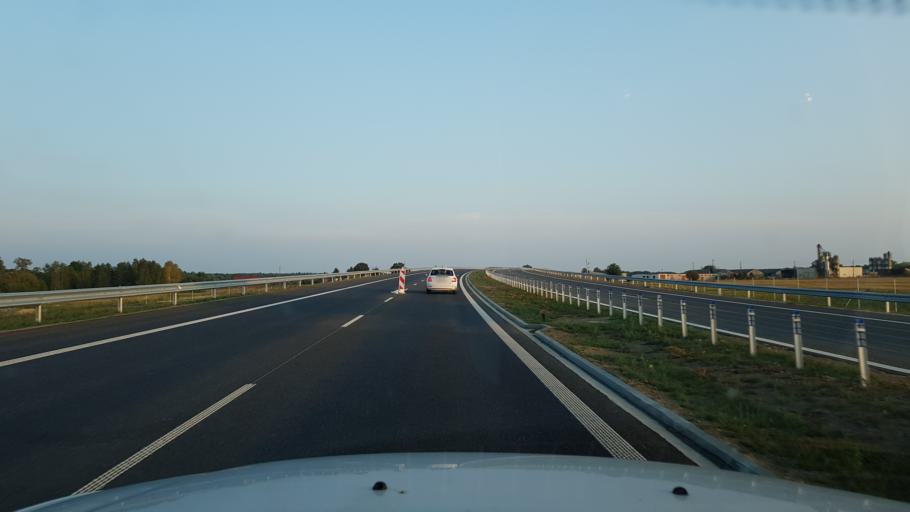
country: PL
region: West Pomeranian Voivodeship
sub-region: Powiat gryficki
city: Ploty
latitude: 53.8018
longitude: 15.2513
